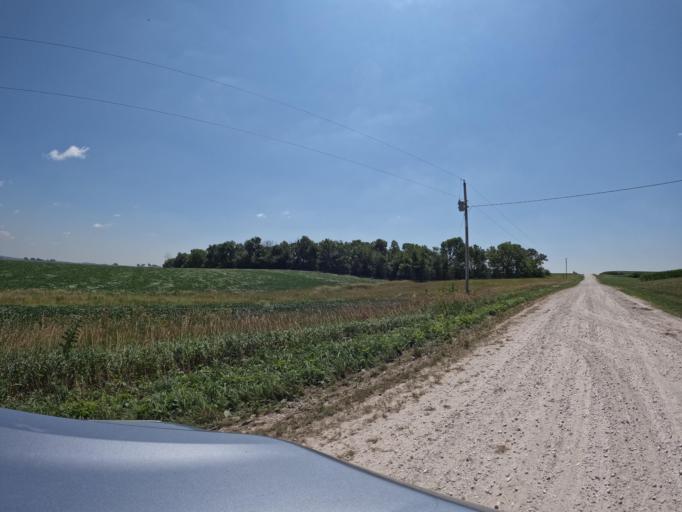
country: US
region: Iowa
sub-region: Keokuk County
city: Sigourney
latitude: 41.2836
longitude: -92.2381
